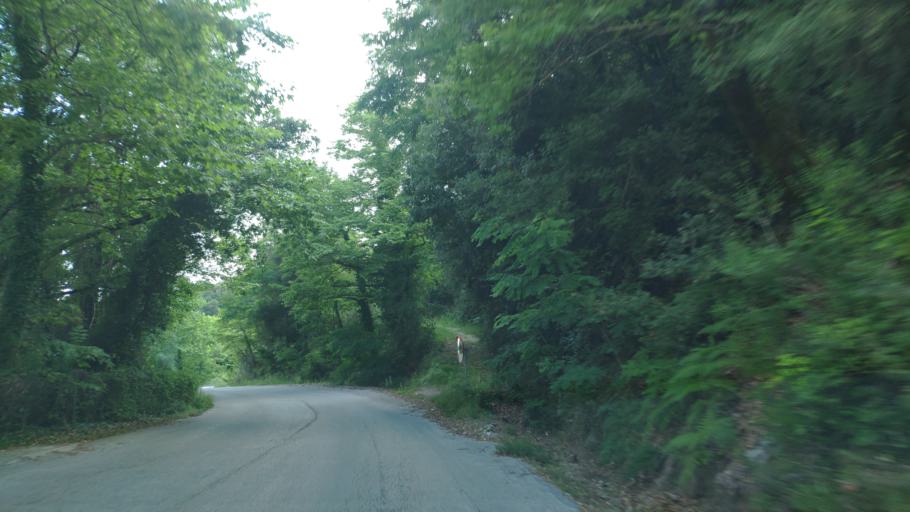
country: GR
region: Epirus
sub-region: Nomos Artas
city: Agios Dimitrios
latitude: 39.3777
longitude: 21.0256
